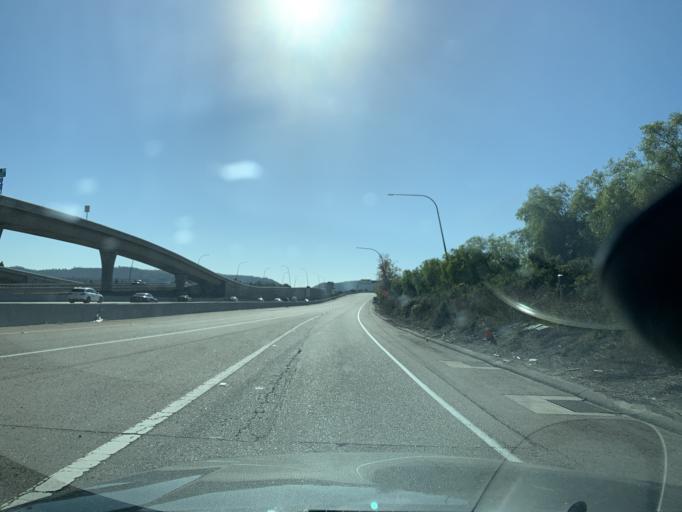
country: US
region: California
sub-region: San Diego County
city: Poway
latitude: 32.9630
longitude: -117.0971
